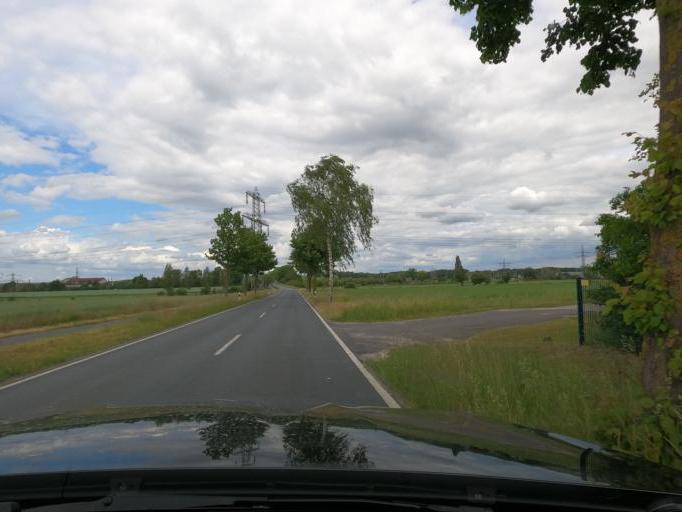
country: DE
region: Lower Saxony
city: Lehrte
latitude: 52.3737
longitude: 9.9236
